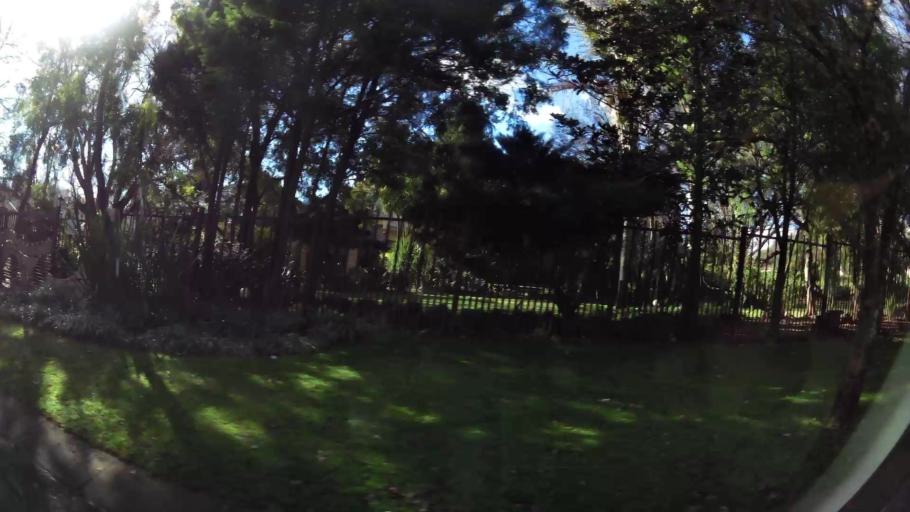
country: ZA
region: North-West
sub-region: Dr Kenneth Kaunda District Municipality
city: Klerksdorp
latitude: -26.8283
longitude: 26.6732
